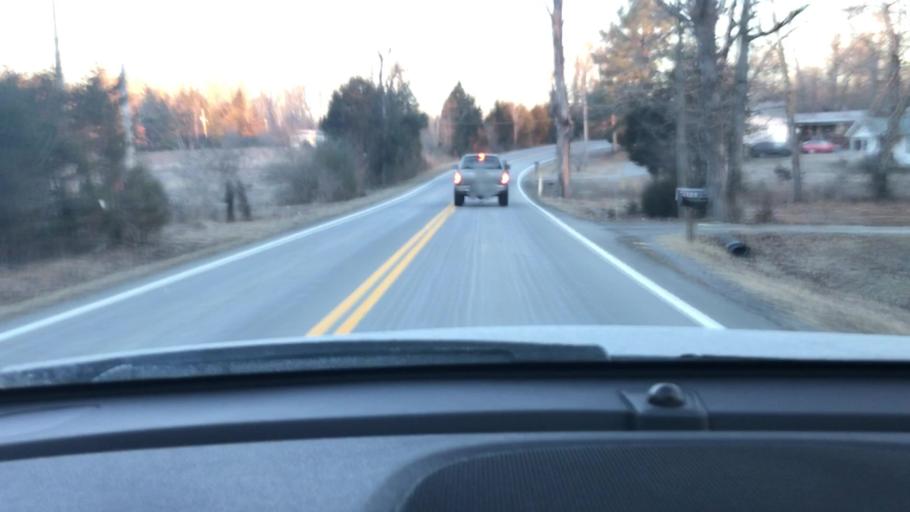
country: US
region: Tennessee
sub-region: Dickson County
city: Charlotte
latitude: 36.2214
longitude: -87.2602
